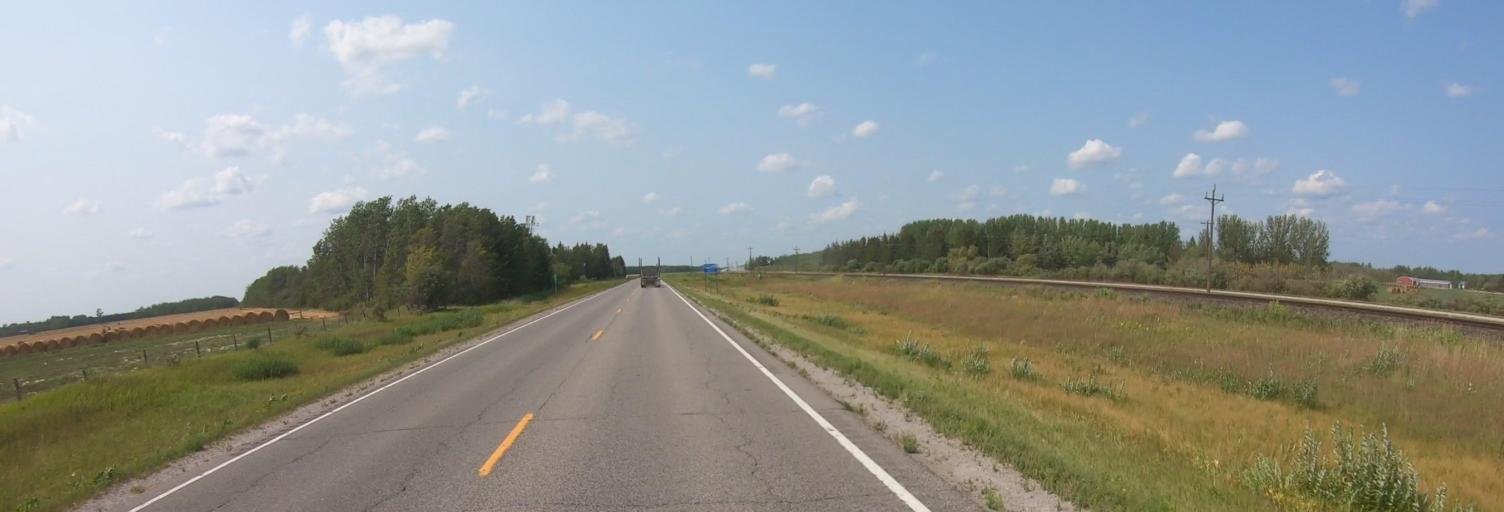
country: US
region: Minnesota
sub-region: Roseau County
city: Warroad
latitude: 48.8721
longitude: -95.2681
